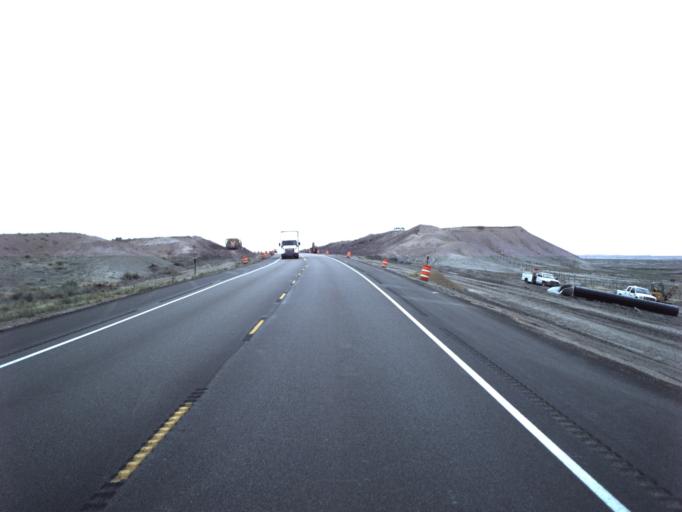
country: US
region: Utah
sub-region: Carbon County
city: East Carbon City
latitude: 39.0356
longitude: -110.3062
